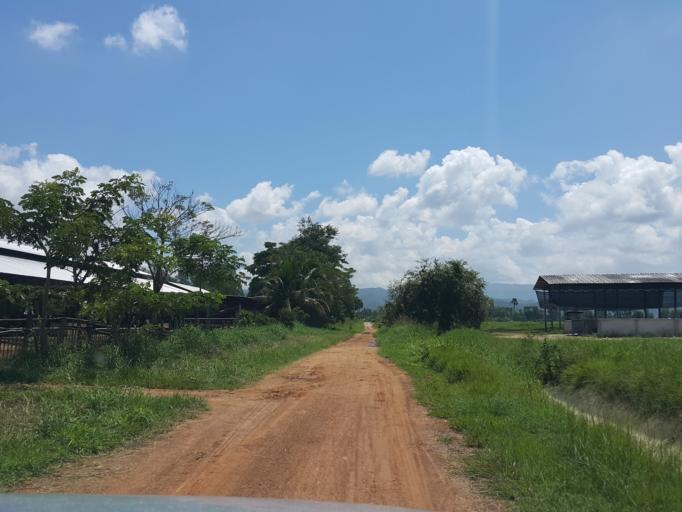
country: TH
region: Lamphun
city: Ban Thi
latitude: 18.6713
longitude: 99.1451
